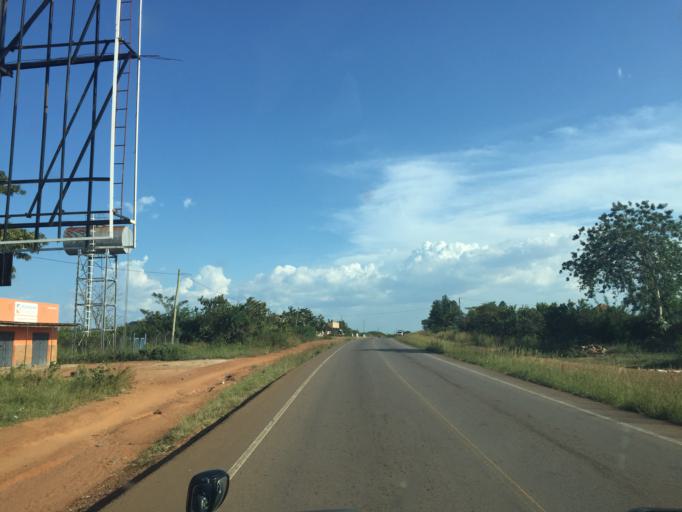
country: UG
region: Central Region
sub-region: Nakasongola District
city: Nakasongola
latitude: 1.2493
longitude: 32.4599
